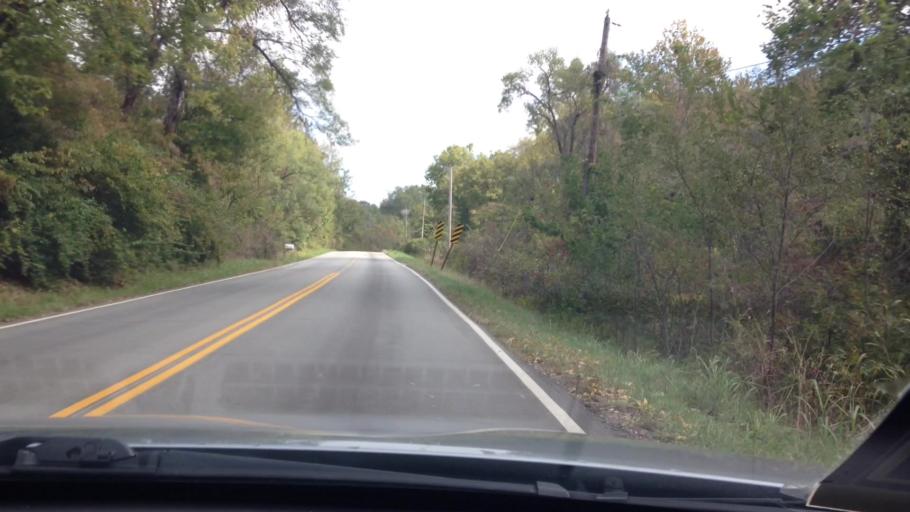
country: US
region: Missouri
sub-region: Platte County
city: Weatherby Lake
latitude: 39.2484
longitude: -94.7902
